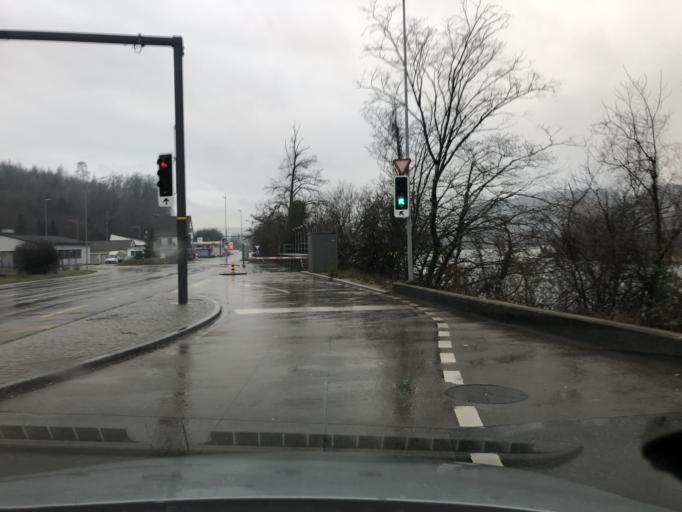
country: CH
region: Aargau
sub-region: Bezirk Zurzach
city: Koblenz
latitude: 47.6074
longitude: 8.2332
